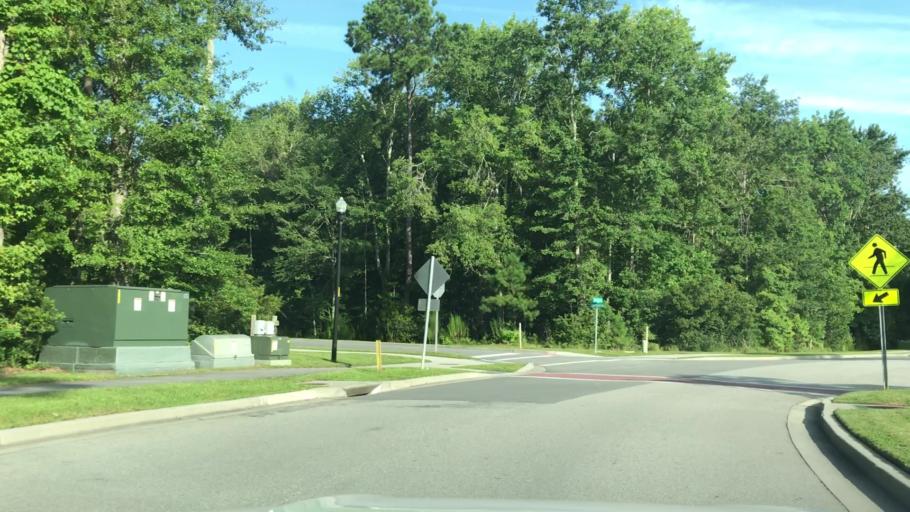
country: US
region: South Carolina
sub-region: Charleston County
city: Isle of Palms
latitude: 32.8896
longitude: -79.7488
